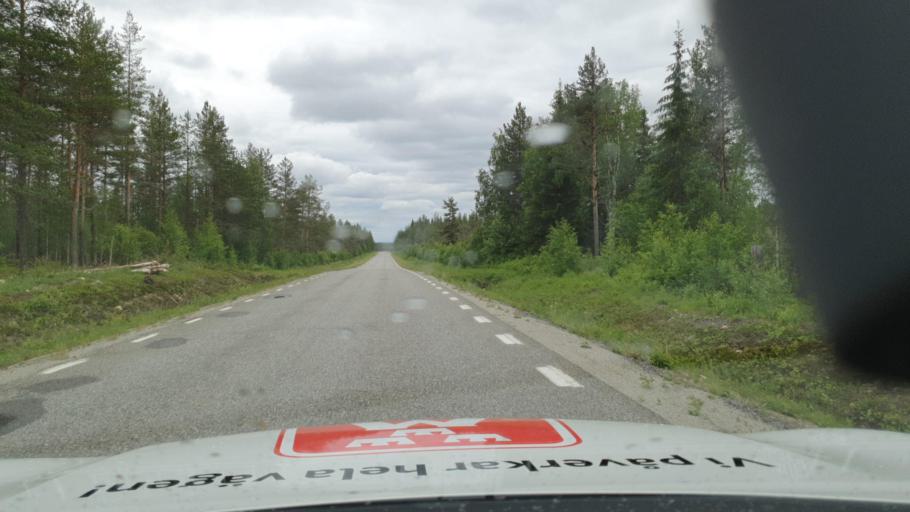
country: SE
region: Vaesterbotten
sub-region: Lycksele Kommun
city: Soderfors
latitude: 64.2662
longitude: 18.2034
